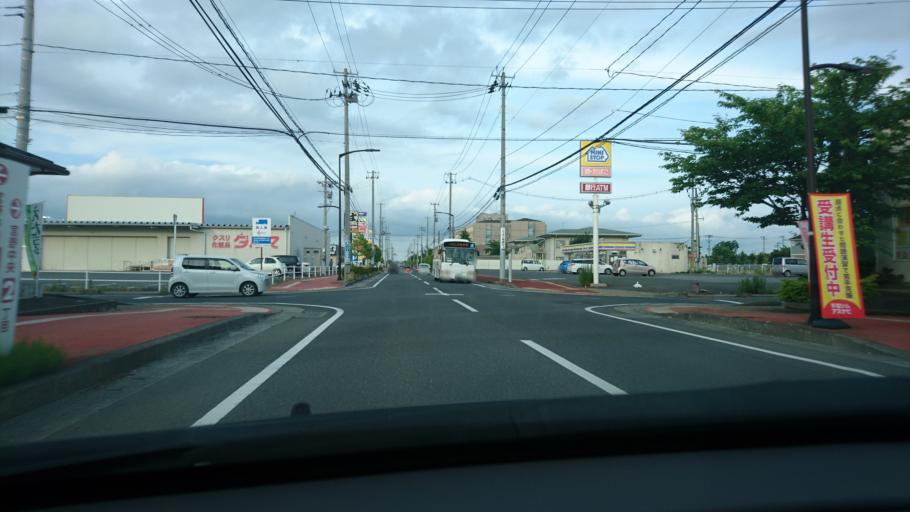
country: JP
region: Miyagi
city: Furukawa
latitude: 38.7466
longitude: 141.0168
